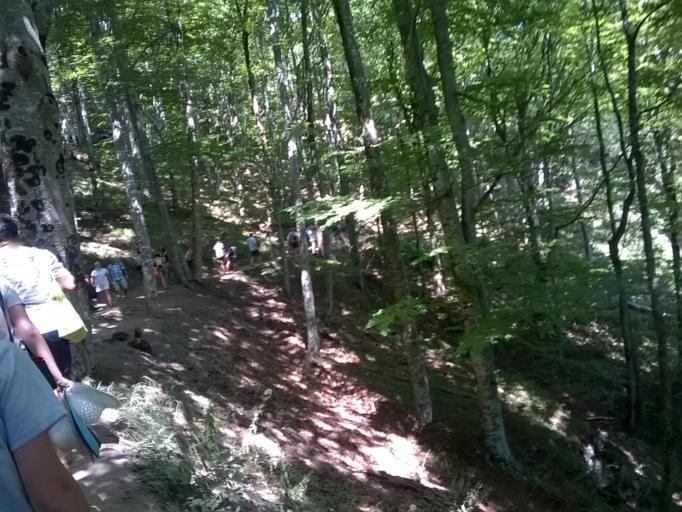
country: HR
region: Licko-Senjska
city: Jezerce
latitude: 44.8750
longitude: 15.6033
